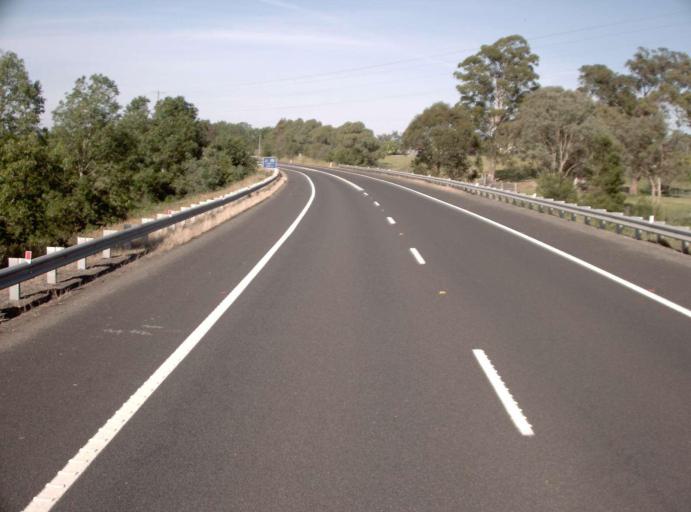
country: AU
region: Victoria
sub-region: East Gippsland
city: Lakes Entrance
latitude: -37.7097
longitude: 148.4619
